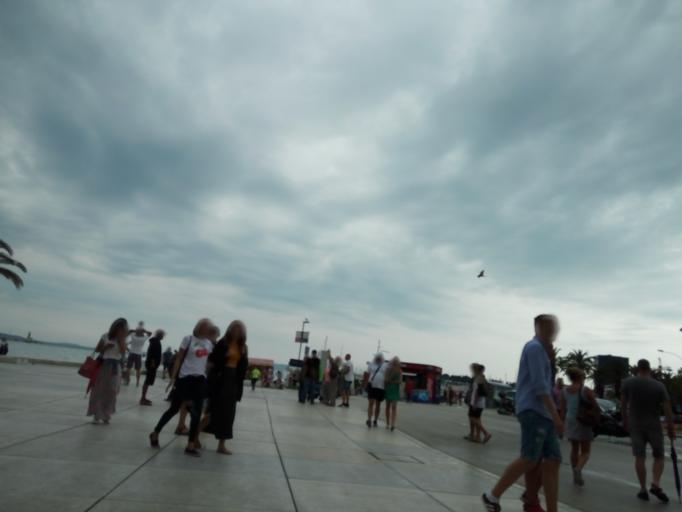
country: HR
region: Splitsko-Dalmatinska
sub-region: Grad Split
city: Split
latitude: 43.5086
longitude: 16.4367
